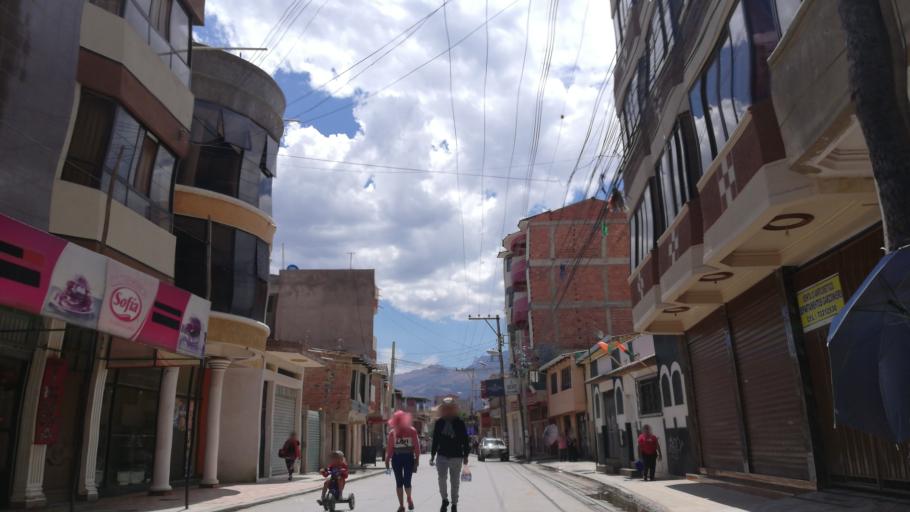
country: BO
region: Cochabamba
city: Cochabamba
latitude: -17.3397
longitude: -66.2177
